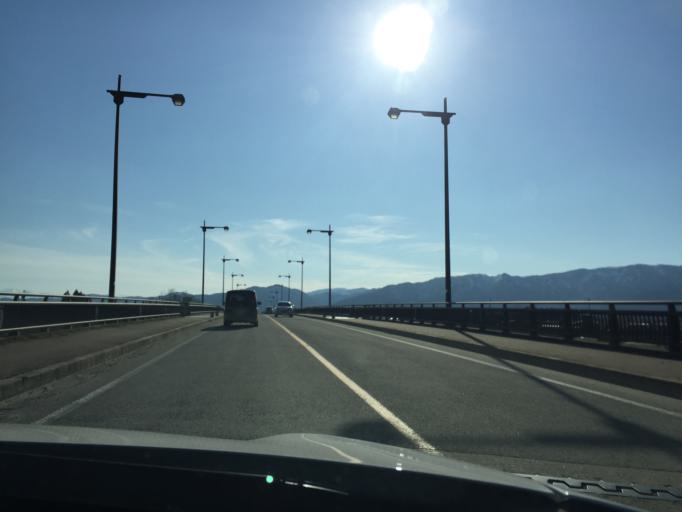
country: JP
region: Yamagata
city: Nagai
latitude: 38.1148
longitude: 140.0483
